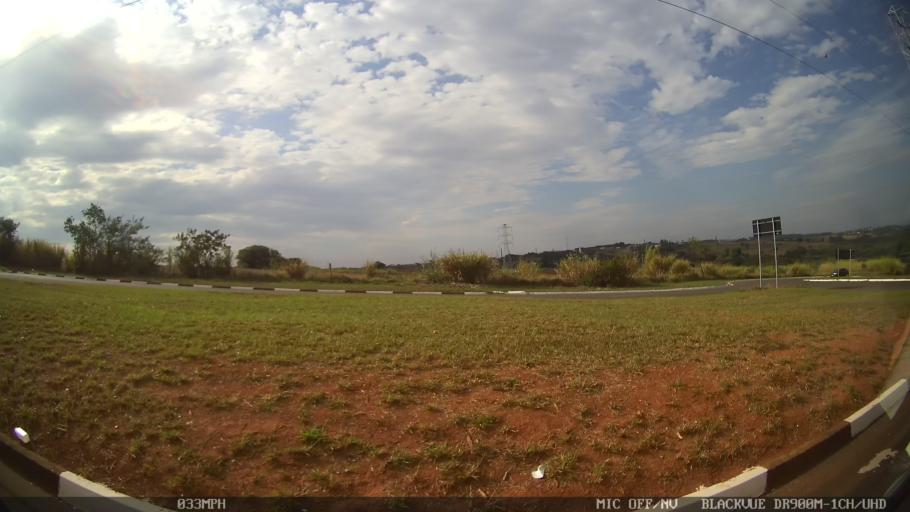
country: BR
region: Sao Paulo
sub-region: Paulinia
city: Paulinia
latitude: -22.7448
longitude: -47.1663
